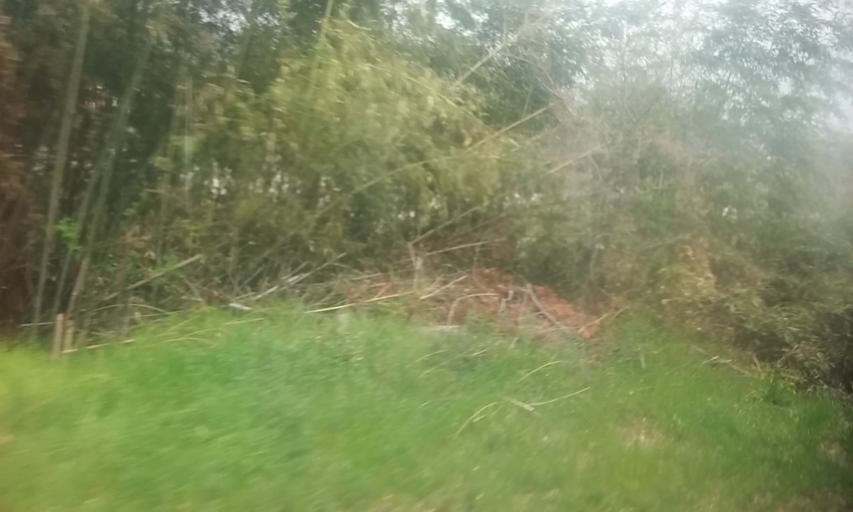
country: JP
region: Gifu
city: Tarui
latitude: 35.3614
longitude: 136.4641
